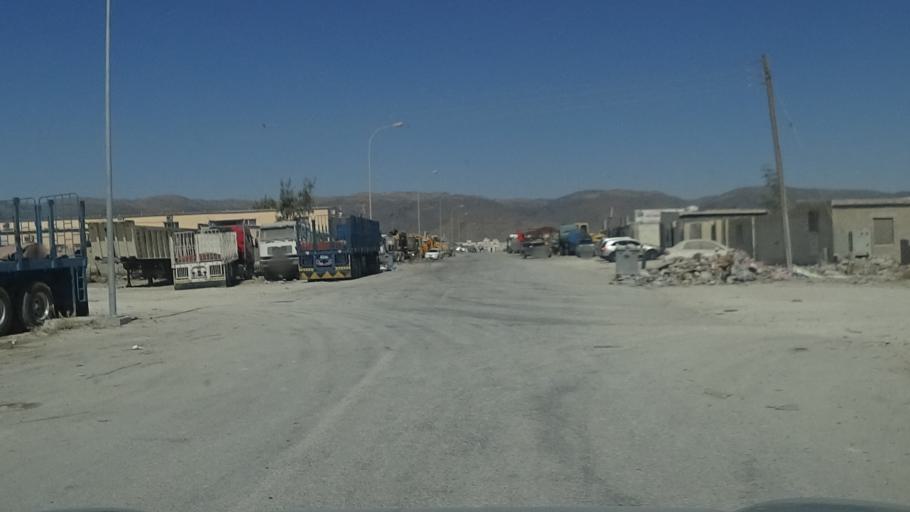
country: OM
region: Zufar
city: Salalah
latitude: 17.0315
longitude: 54.0435
